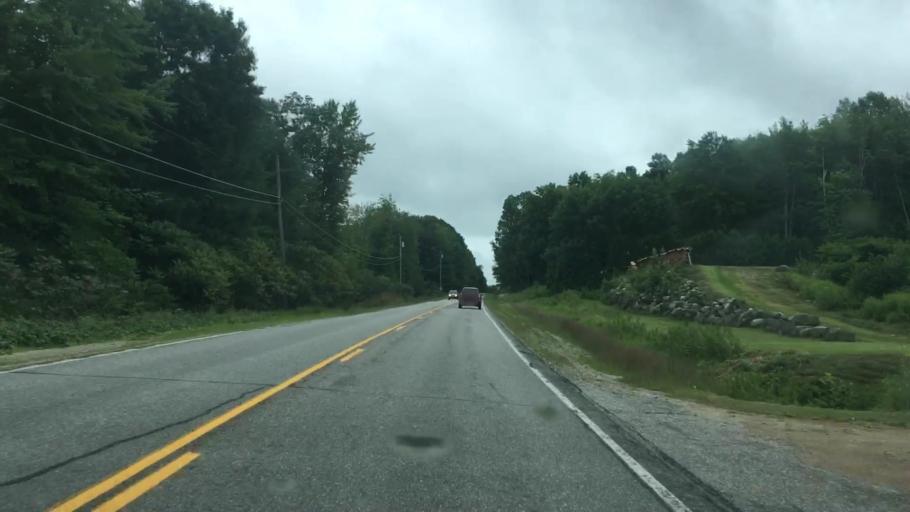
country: US
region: Maine
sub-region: Oxford County
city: Brownfield
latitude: 43.9578
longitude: -70.8986
